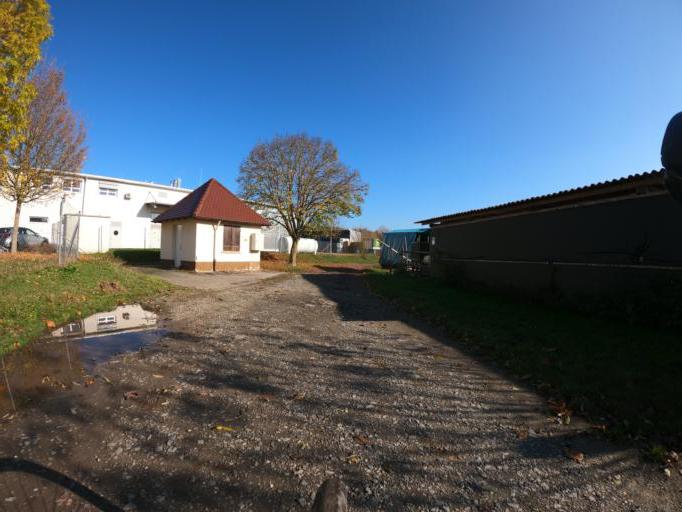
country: DE
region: Baden-Wuerttemberg
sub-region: Regierungsbezirk Stuttgart
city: Magstadt
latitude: 48.7440
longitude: 8.9779
